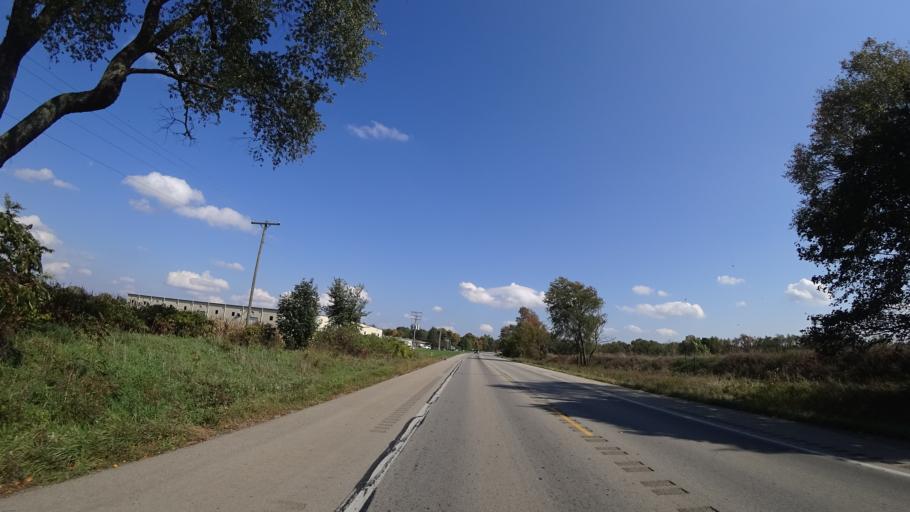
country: US
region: Michigan
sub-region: Calhoun County
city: Homer
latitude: 42.1475
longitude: -84.8231
